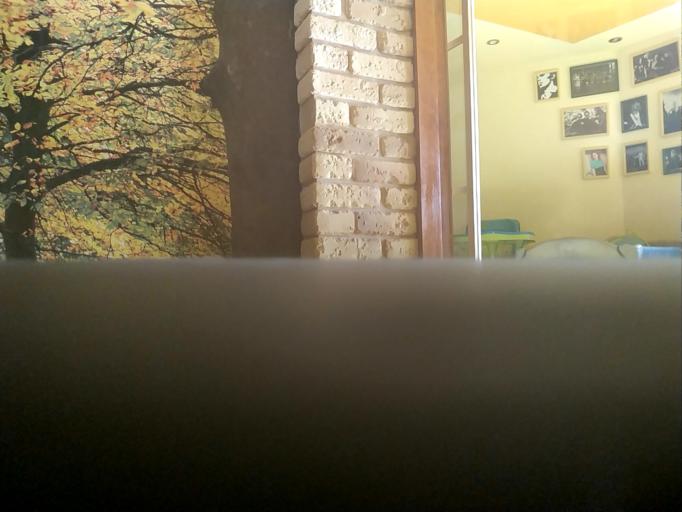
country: RU
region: Smolensk
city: Temkino
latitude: 55.0462
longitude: 34.9201
